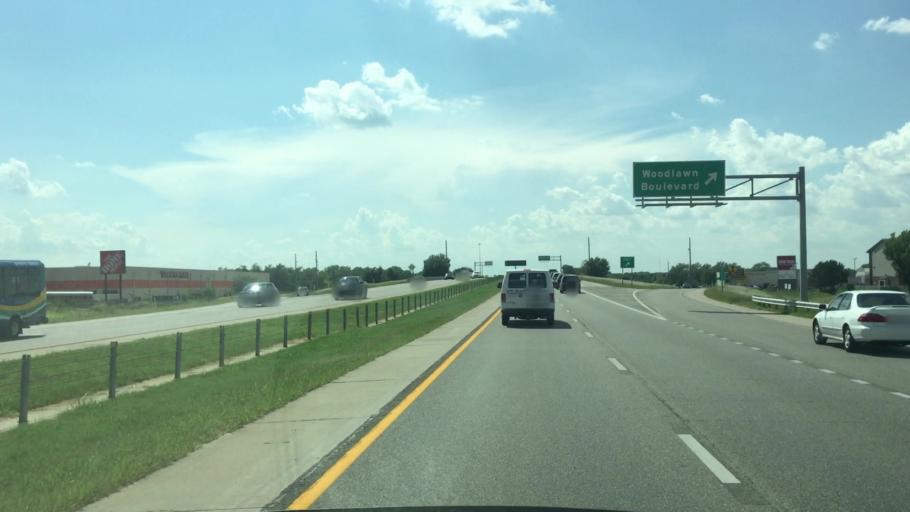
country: US
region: Kansas
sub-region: Sedgwick County
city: Bellaire
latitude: 37.7455
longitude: -97.2582
